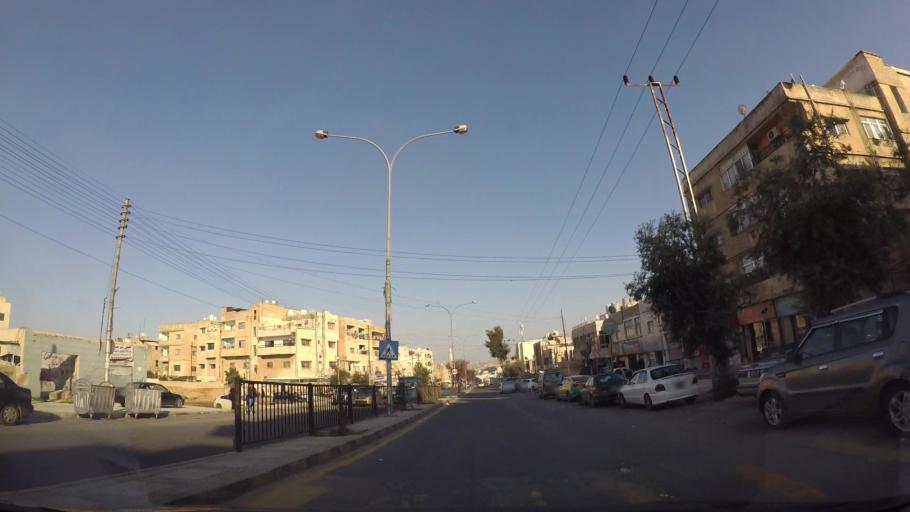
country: JO
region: Amman
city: Amman
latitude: 31.9752
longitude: 35.9609
